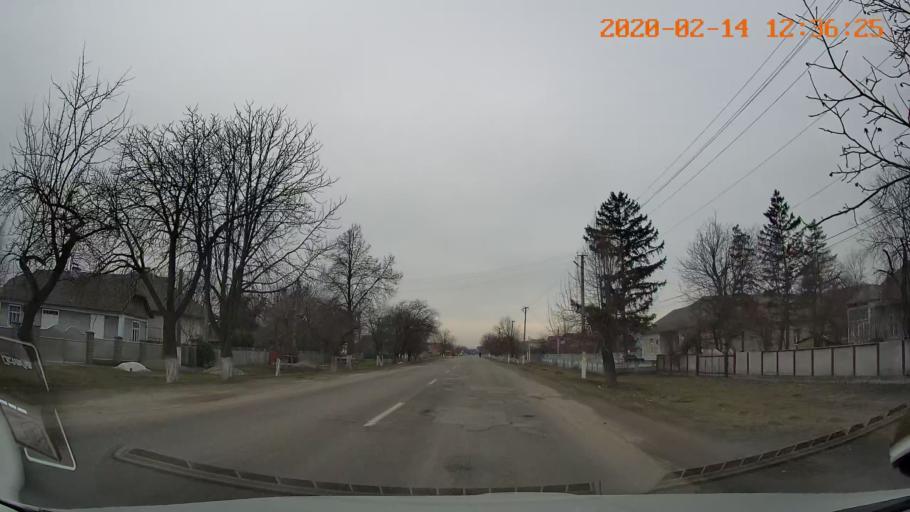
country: RO
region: Botosani
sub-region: Comuna Darabani
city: Bajura
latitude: 48.2235
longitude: 26.4984
